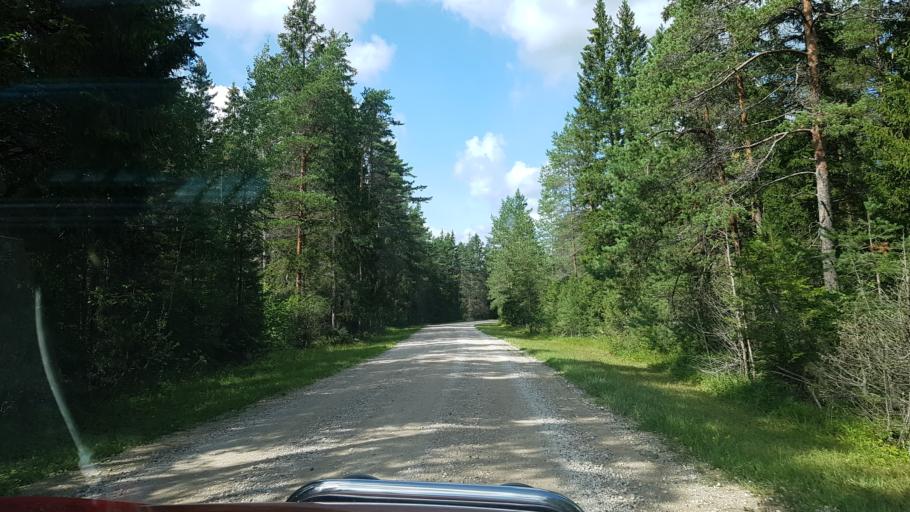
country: EE
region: Raplamaa
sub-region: Rapla vald
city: Rapla
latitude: 58.9587
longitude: 24.6507
